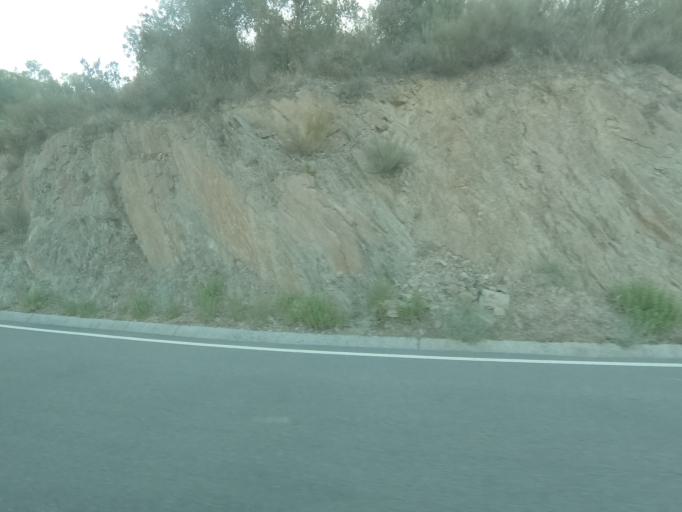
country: PT
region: Viseu
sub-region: Tabuaco
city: Tabuaco
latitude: 41.1509
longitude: -7.6241
